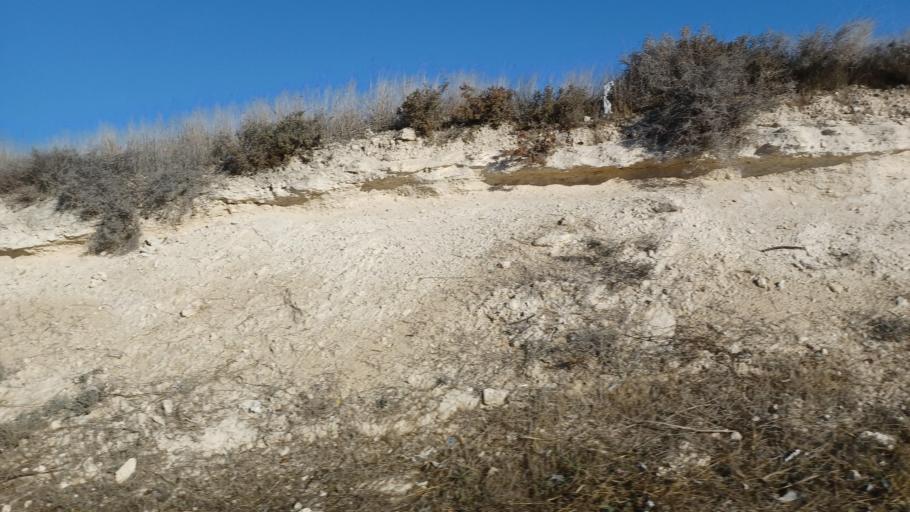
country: CY
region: Larnaka
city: Psevdas
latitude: 34.9701
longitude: 33.5238
